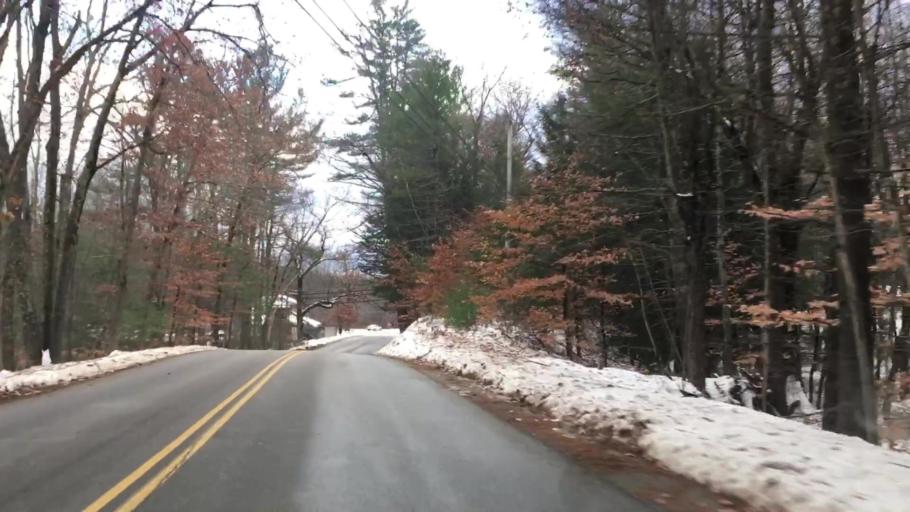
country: US
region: New Hampshire
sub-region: Hillsborough County
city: Mont Vernon
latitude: 42.8983
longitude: -71.6043
